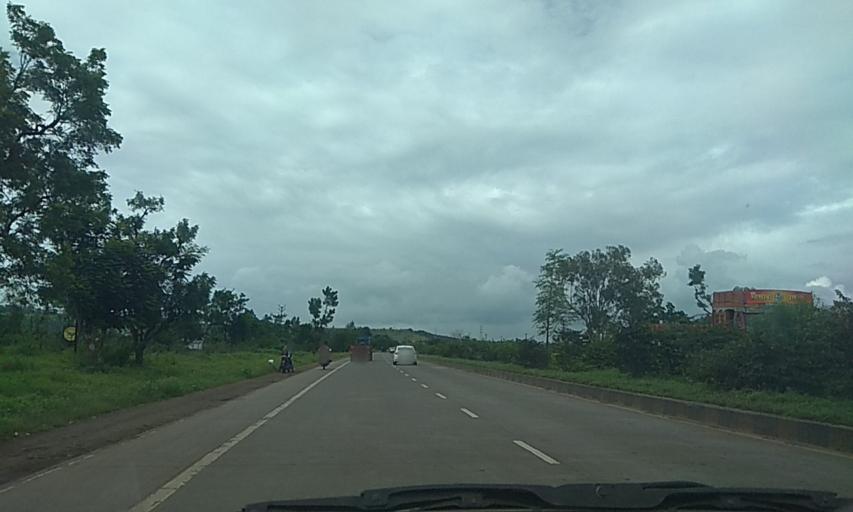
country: IN
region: Maharashtra
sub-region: Kolhapur
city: Kagal
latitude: 16.5916
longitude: 74.3074
